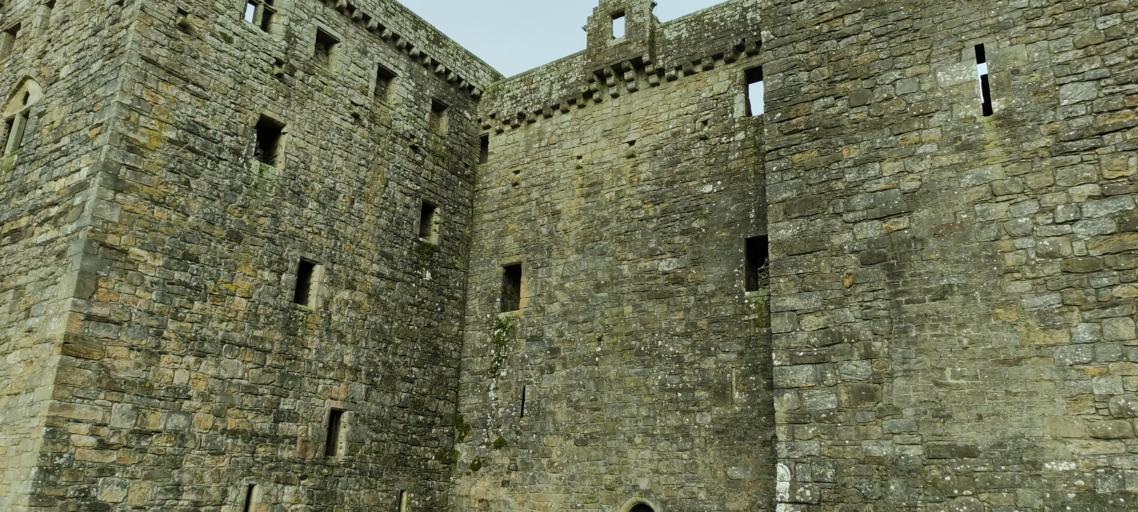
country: GB
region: Scotland
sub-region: The Scottish Borders
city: Hawick
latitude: 55.2558
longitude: -2.7930
